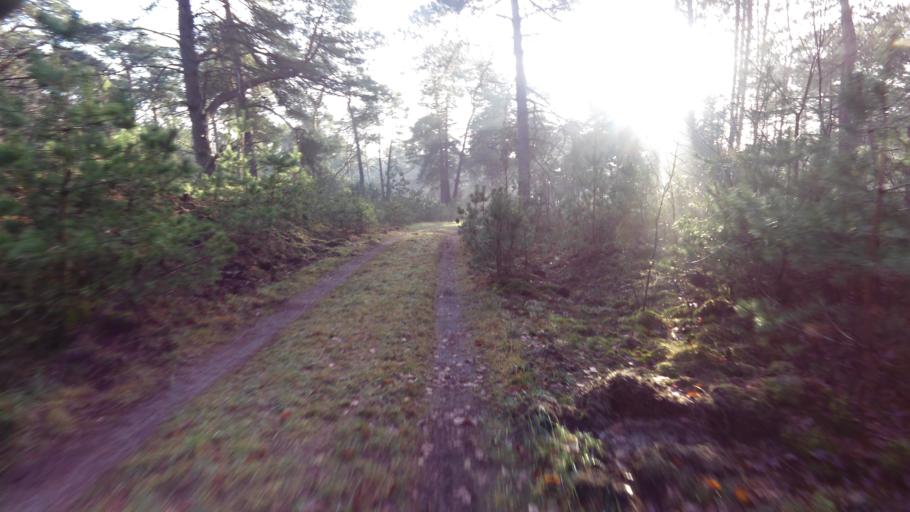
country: NL
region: Gelderland
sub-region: Gemeente Barneveld
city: Garderen
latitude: 52.2009
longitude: 5.7396
